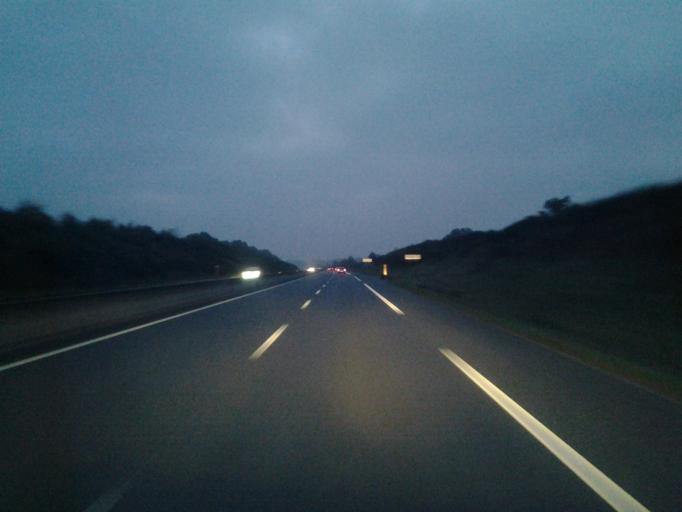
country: FR
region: Pays de la Loire
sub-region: Departement de la Vendee
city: Les Clouzeaux
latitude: 46.6327
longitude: -1.4782
